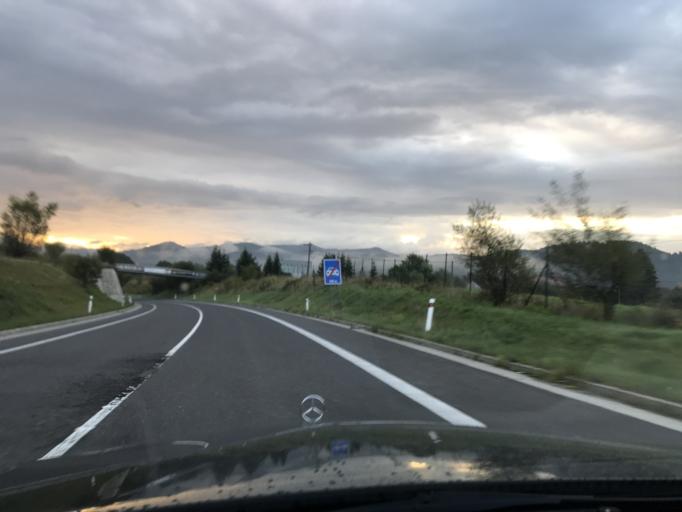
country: SK
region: Zilinsky
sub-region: Okres Dolny Kubin
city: Dolny Kubin
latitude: 49.2587
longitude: 19.4011
